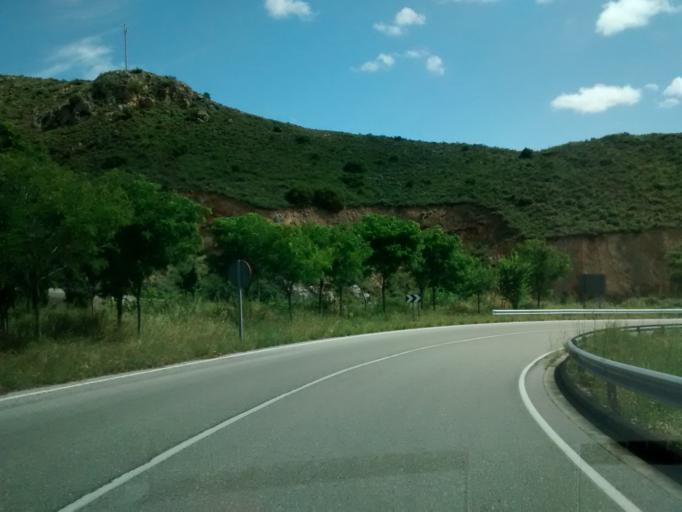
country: ES
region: La Rioja
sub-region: Provincia de La Rioja
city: Leza de Rio Leza
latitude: 42.3333
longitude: -2.4106
